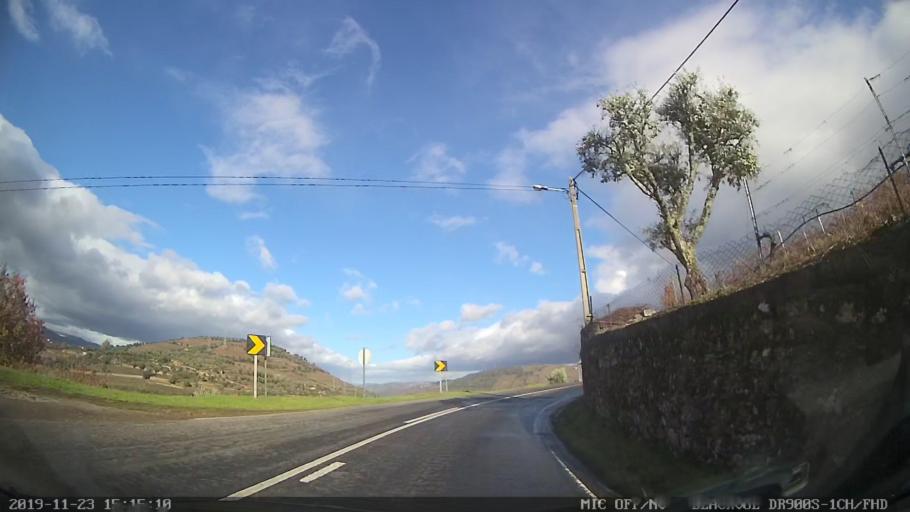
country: PT
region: Viseu
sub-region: Lamego
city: Lamego
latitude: 41.1286
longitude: -7.7922
